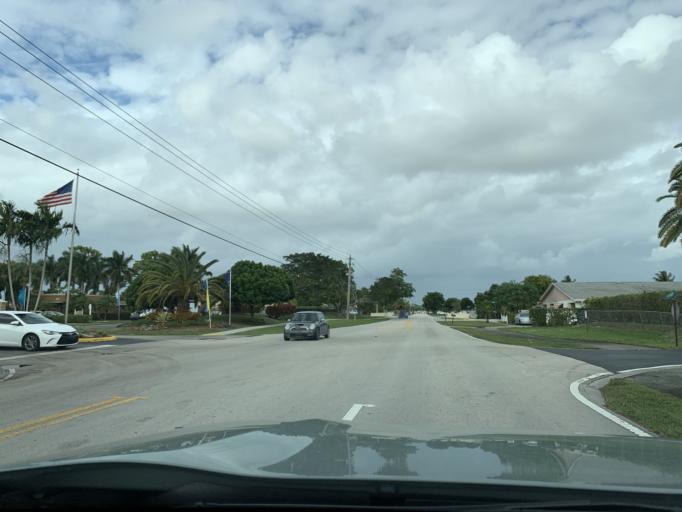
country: US
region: Florida
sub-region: Palm Beach County
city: Greenacres City
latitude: 26.6474
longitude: -80.1369
